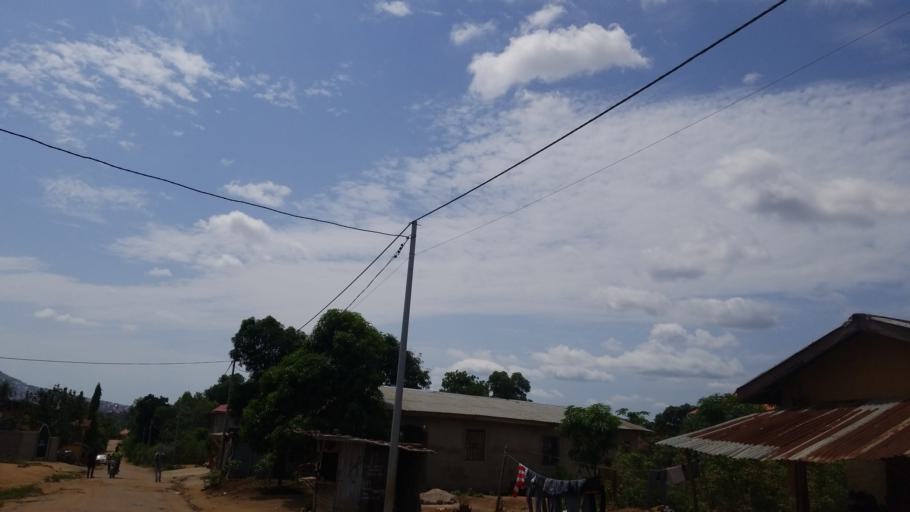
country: SL
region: Western Area
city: Waterloo
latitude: 8.3148
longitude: -13.0565
